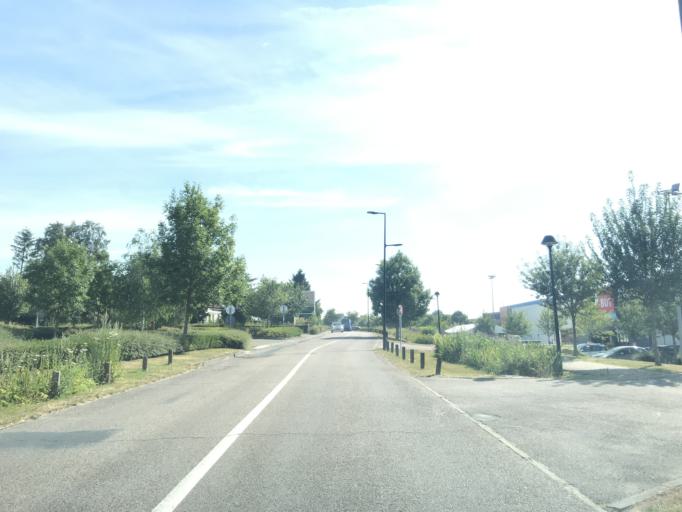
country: FR
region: Haute-Normandie
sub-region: Departement de la Seine-Maritime
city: Roumare
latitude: 49.5270
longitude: 0.9662
